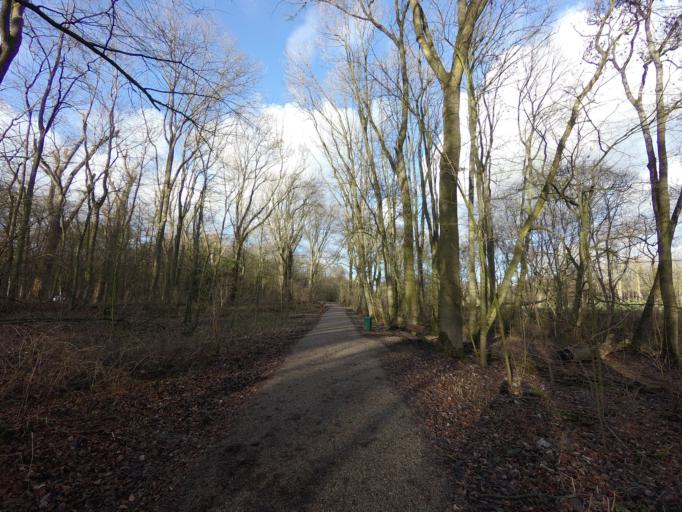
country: NL
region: South Holland
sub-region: Gemeente Rotterdam
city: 's-Gravenland
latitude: 51.9324
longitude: 4.5299
